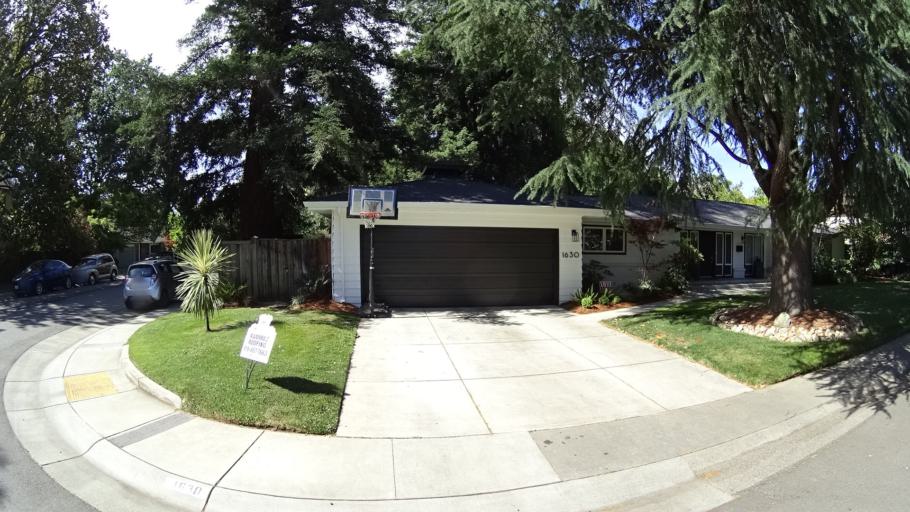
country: US
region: California
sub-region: Sacramento County
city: Sacramento
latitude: 38.5345
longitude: -121.4992
